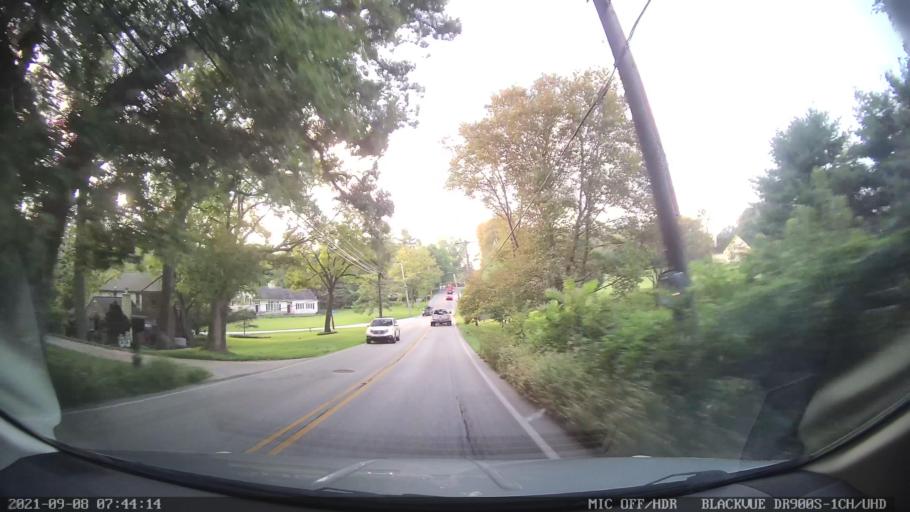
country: US
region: Pennsylvania
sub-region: Delaware County
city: Radnor
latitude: 40.0623
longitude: -75.3743
